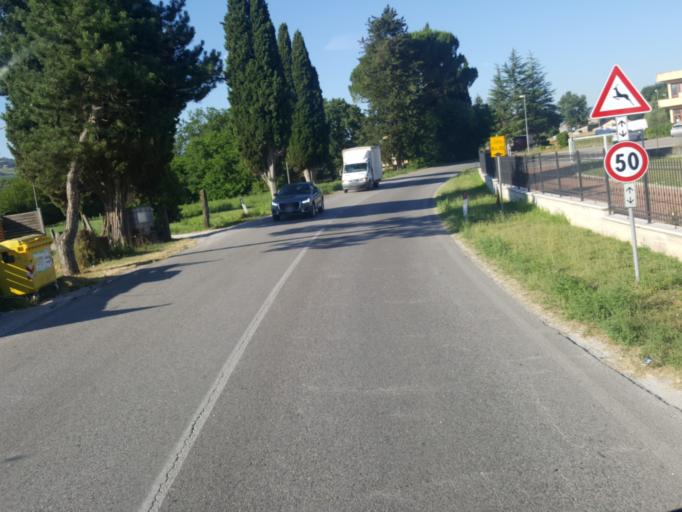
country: IT
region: The Marches
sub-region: Provincia di Pesaro e Urbino
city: Borgo Massano
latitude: 43.8242
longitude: 12.6808
